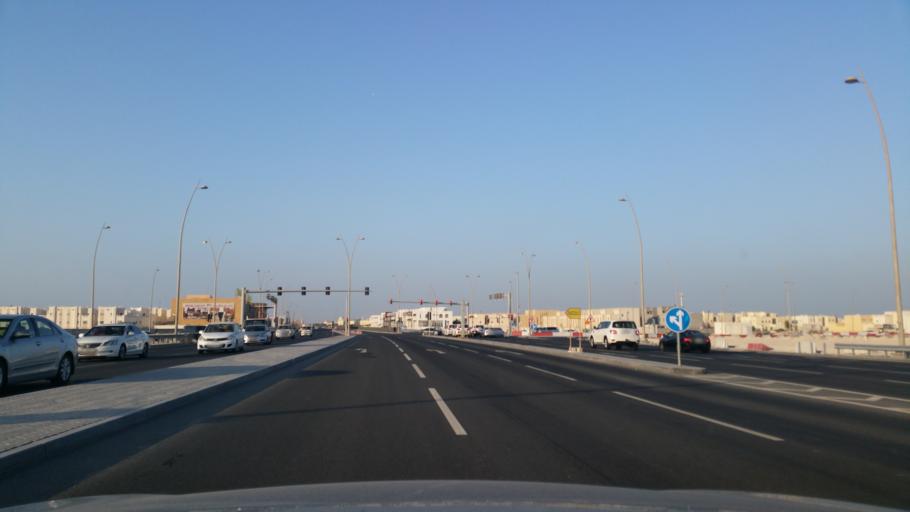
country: QA
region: Al Khawr
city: Al Khawr
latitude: 25.6624
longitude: 51.5007
